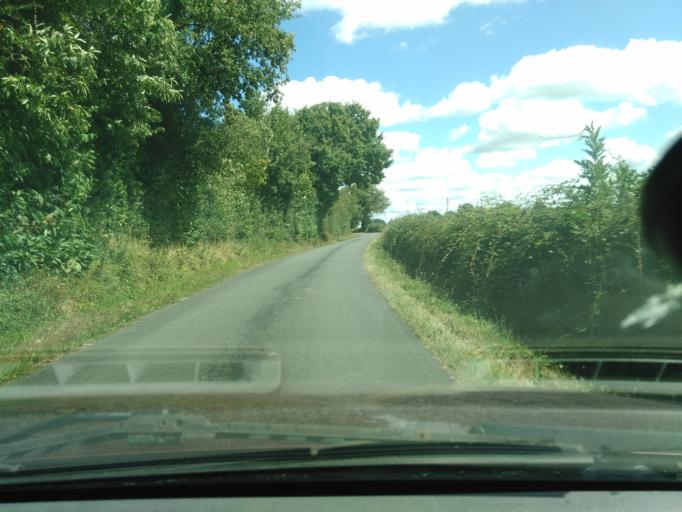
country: FR
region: Pays de la Loire
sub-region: Departement de la Vendee
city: Dompierre-sur-Yon
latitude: 46.7409
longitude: -1.3696
